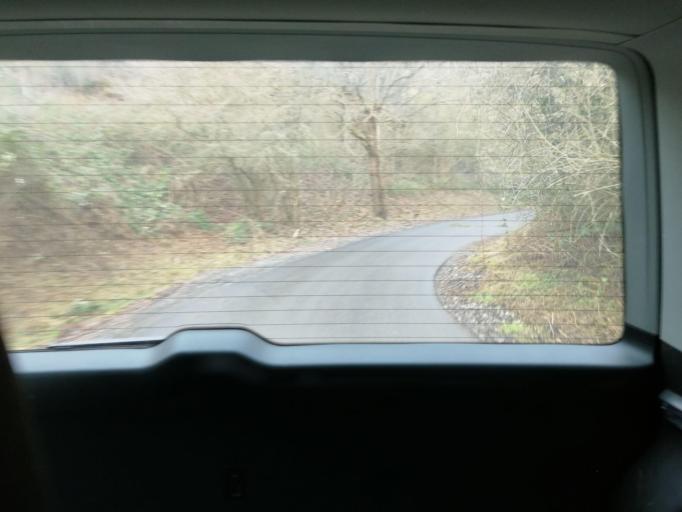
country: DE
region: Rheinland-Pfalz
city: Mayschoss
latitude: 50.5301
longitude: 7.0217
